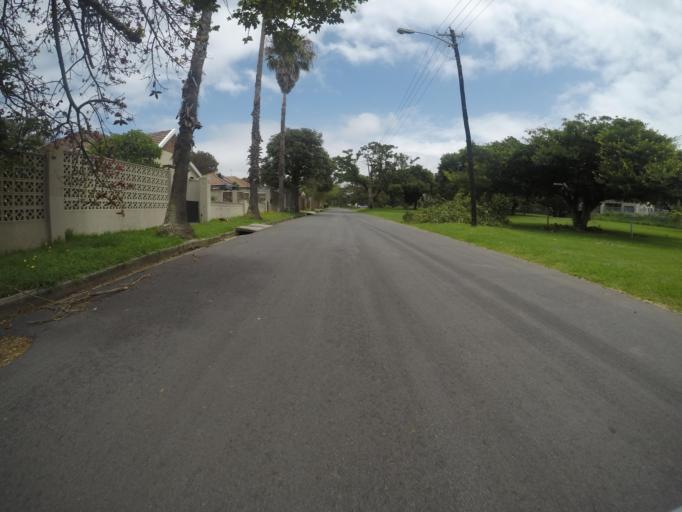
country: ZA
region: Eastern Cape
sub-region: Buffalo City Metropolitan Municipality
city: East London
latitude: -32.9902
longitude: 27.9287
